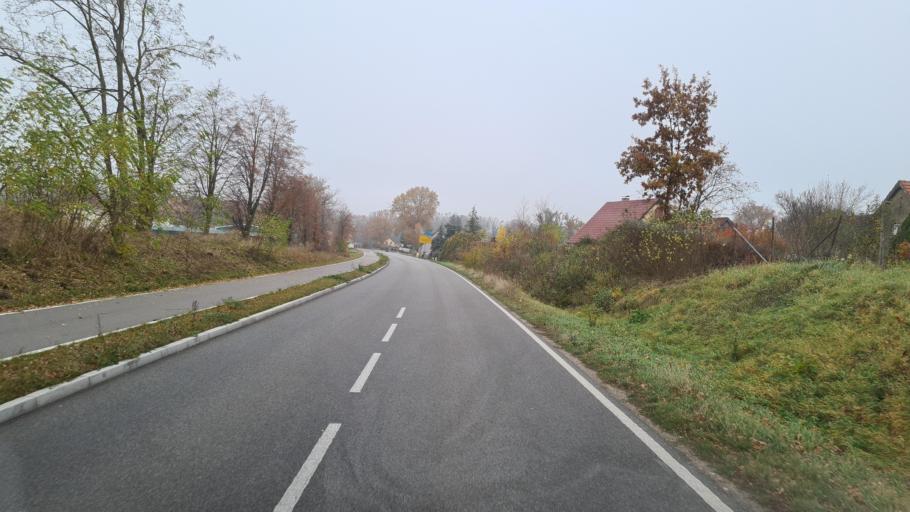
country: DE
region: Brandenburg
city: Gross Kreutz
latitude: 52.4012
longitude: 12.7708
